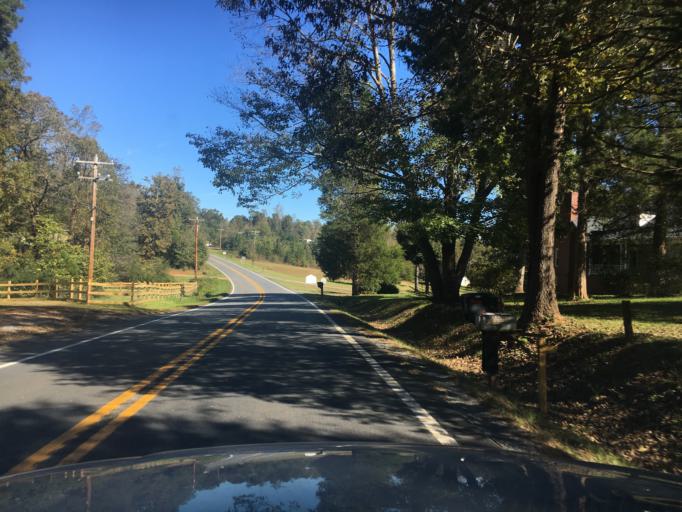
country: US
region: North Carolina
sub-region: Rutherford County
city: Spindale
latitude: 35.4527
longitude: -81.8877
